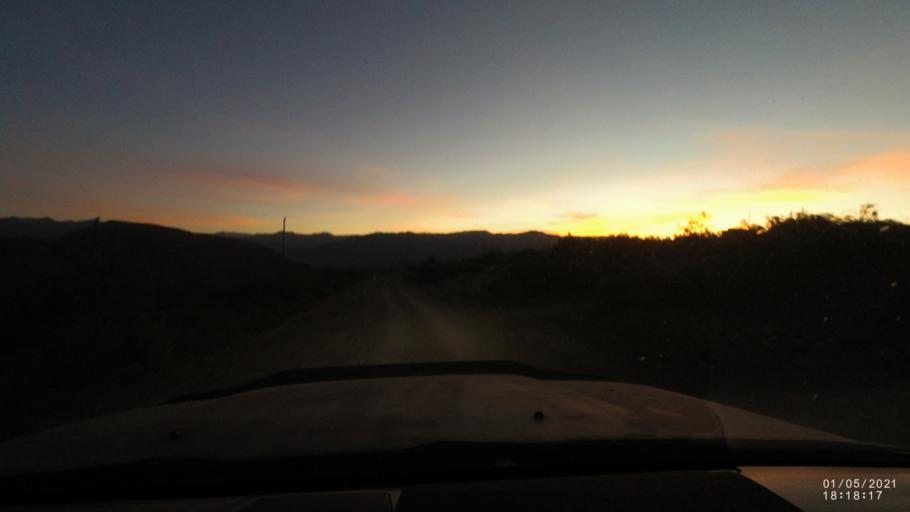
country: BO
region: Cochabamba
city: Capinota
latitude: -17.6654
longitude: -66.2202
